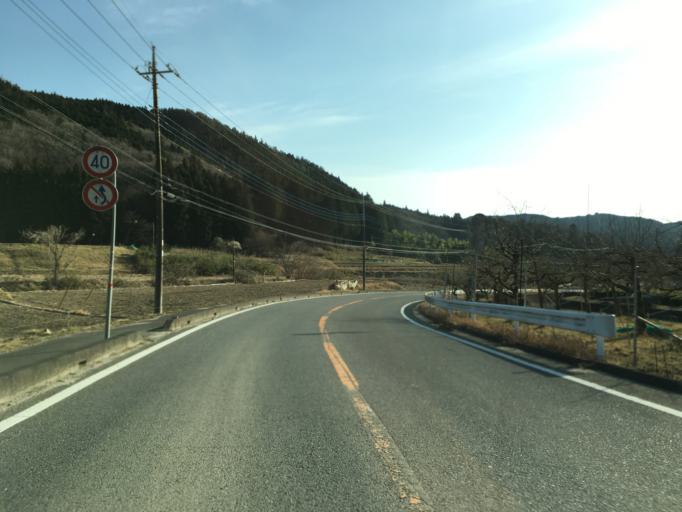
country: JP
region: Ibaraki
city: Daigo
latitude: 36.7211
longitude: 140.5071
